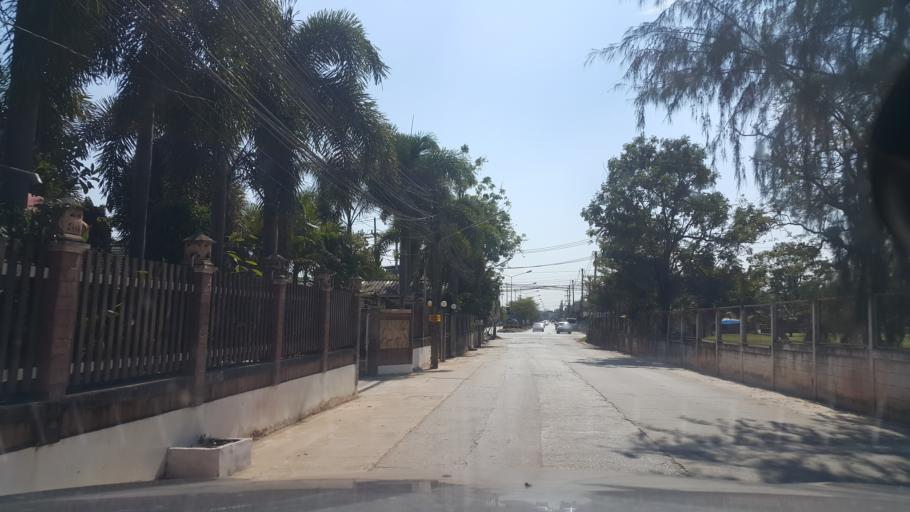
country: TH
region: Changwat Udon Thani
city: Udon Thani
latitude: 17.4505
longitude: 102.7829
